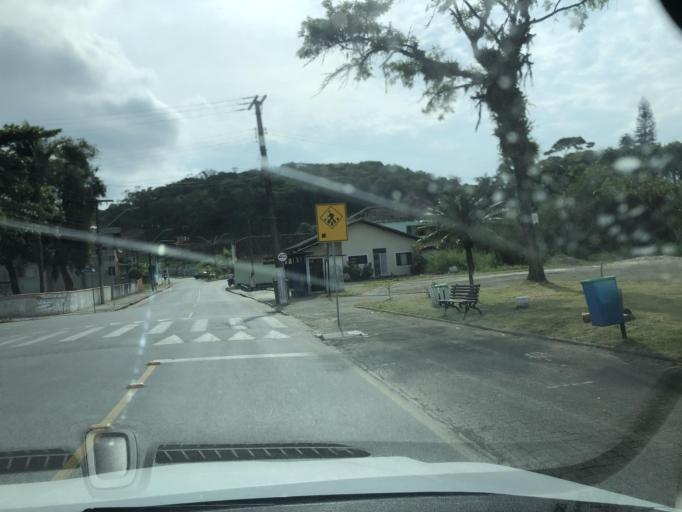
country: BR
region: Santa Catarina
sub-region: Sao Francisco Do Sul
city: Sao Francisco do Sul
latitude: -26.2316
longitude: -48.6234
